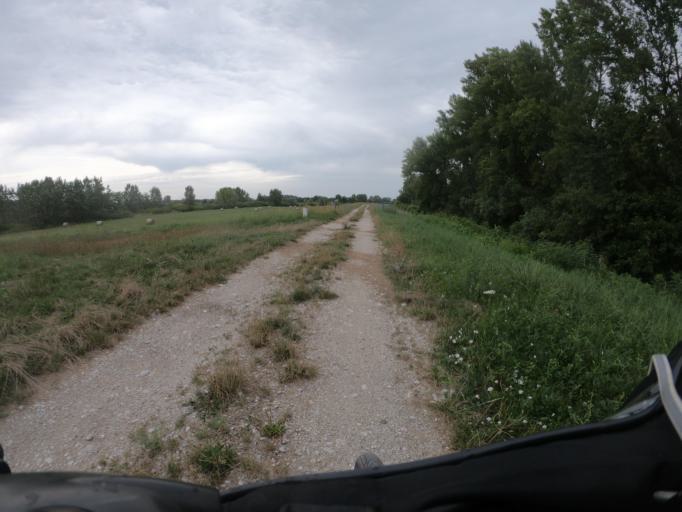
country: HU
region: Jasz-Nagykun-Szolnok
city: Tiszafured
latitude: 47.6845
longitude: 20.7840
